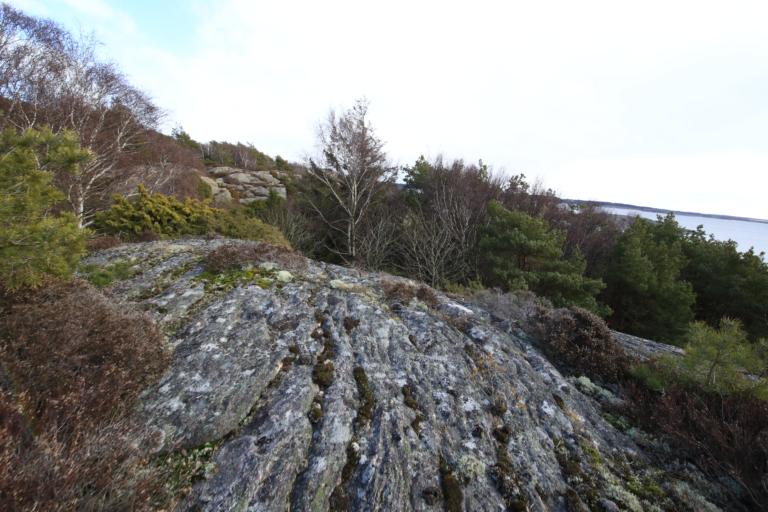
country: SE
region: Halland
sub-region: Kungsbacka Kommun
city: Frillesas
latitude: 57.2148
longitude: 12.1434
